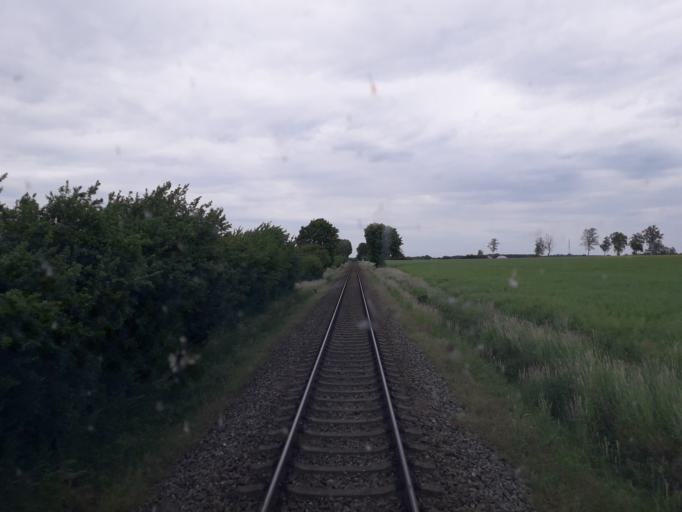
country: DE
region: Brandenburg
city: Neuruppin
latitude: 52.8933
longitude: 12.8496
